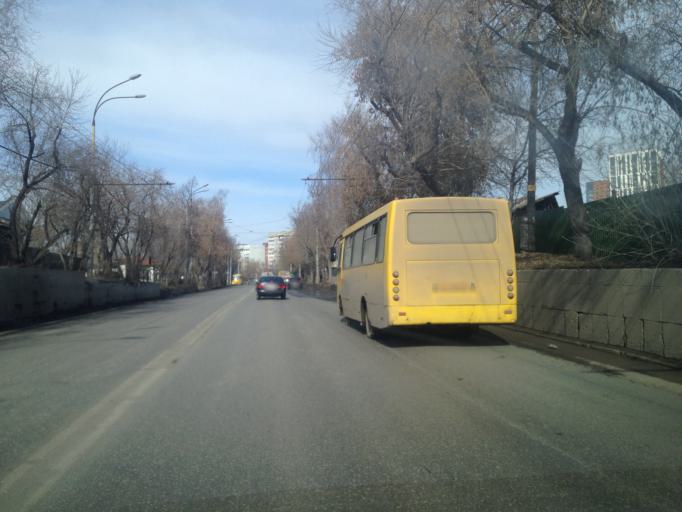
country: RU
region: Sverdlovsk
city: Yekaterinburg
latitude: 56.8046
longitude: 60.5892
